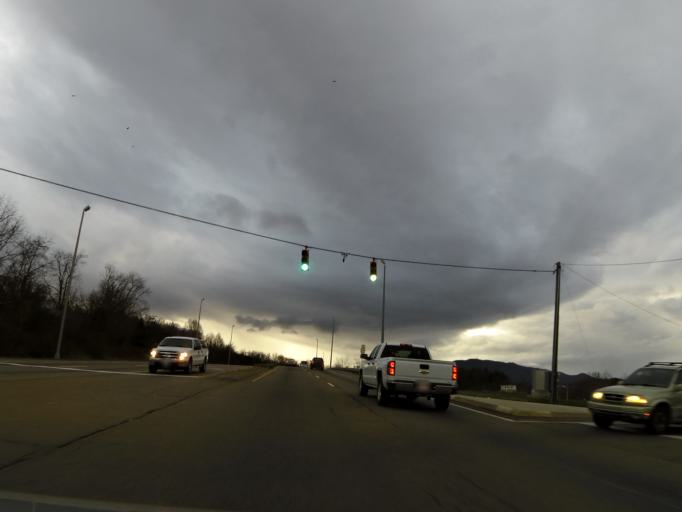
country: US
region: Tennessee
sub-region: Carter County
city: Central
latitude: 36.3211
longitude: -82.2738
